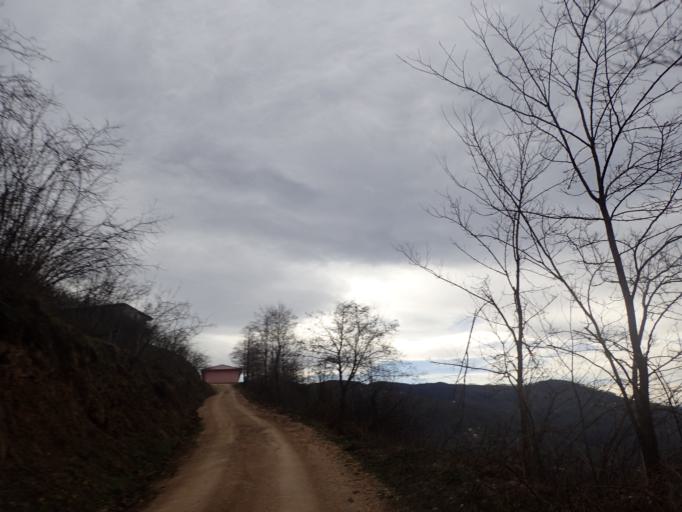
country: TR
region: Ordu
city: Camas
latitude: 40.8883
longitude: 37.5150
